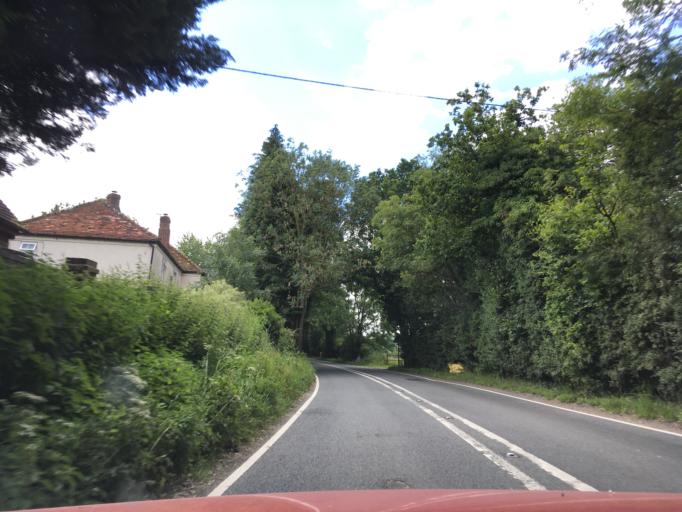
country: GB
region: England
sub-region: Hampshire
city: Highclere
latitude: 51.3347
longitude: -1.3778
